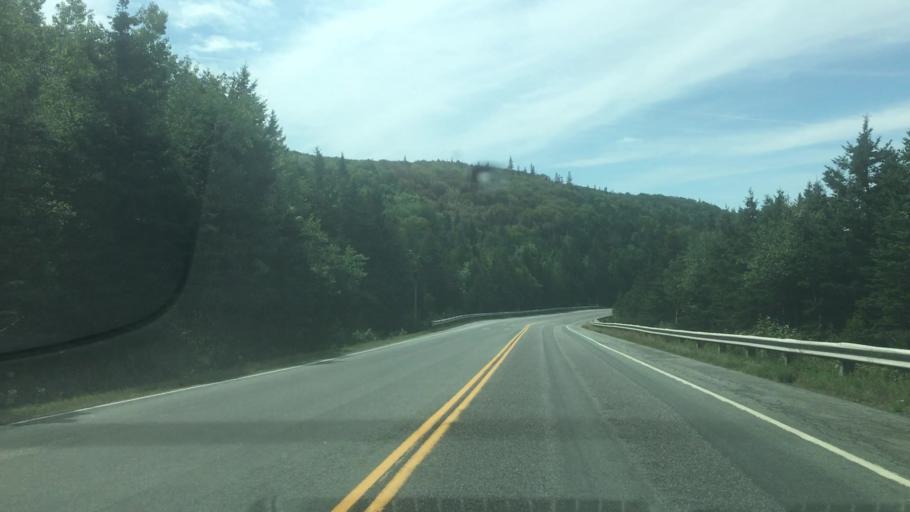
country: CA
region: Nova Scotia
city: Sydney Mines
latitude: 46.2417
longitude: -60.5602
